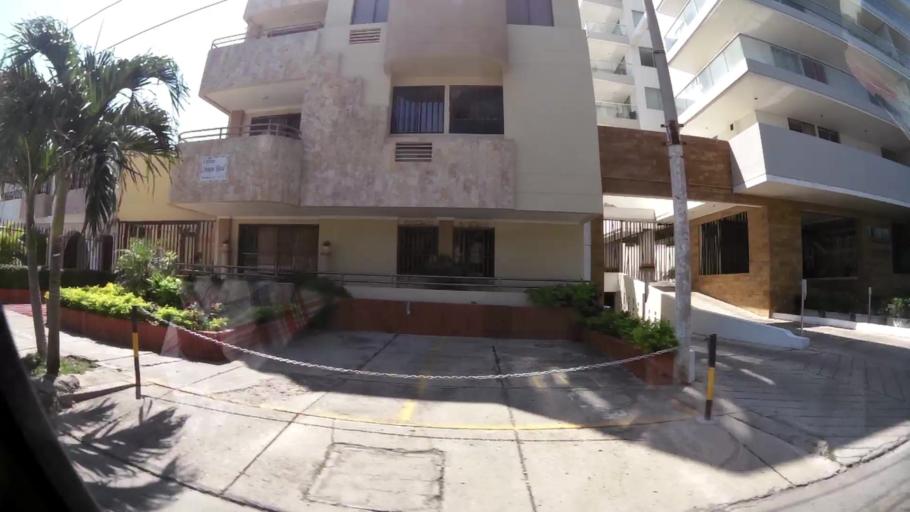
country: CO
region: Bolivar
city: Cartagena
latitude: 10.4448
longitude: -75.5210
